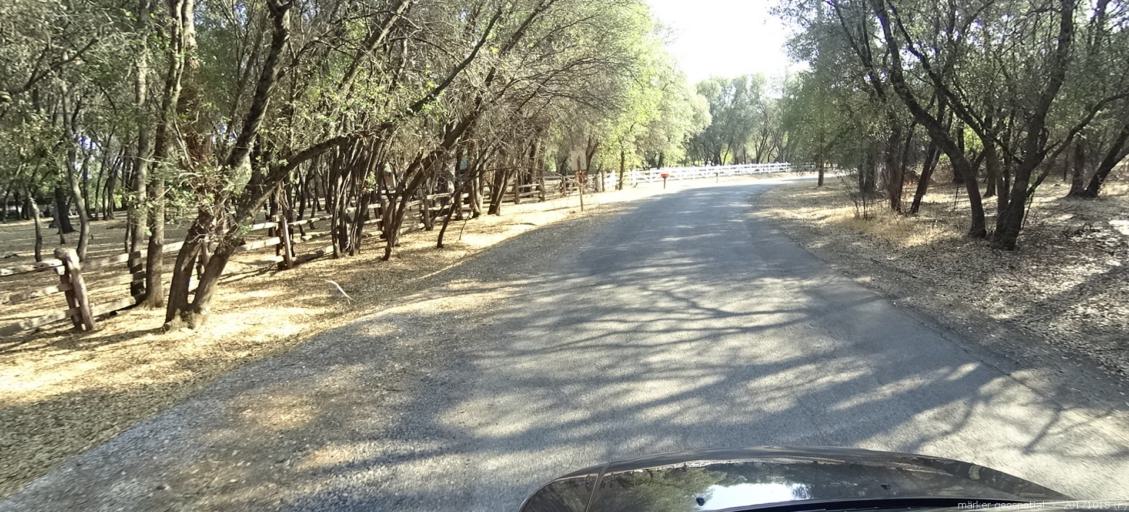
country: US
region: California
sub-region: Shasta County
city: Palo Cedro
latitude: 40.5786
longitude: -122.2279
